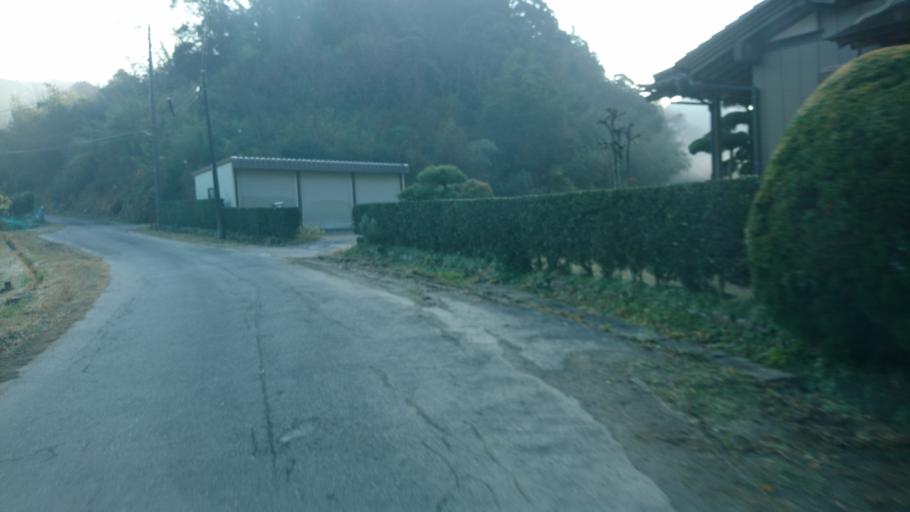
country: JP
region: Chiba
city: Kimitsu
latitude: 35.2904
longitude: 139.9519
